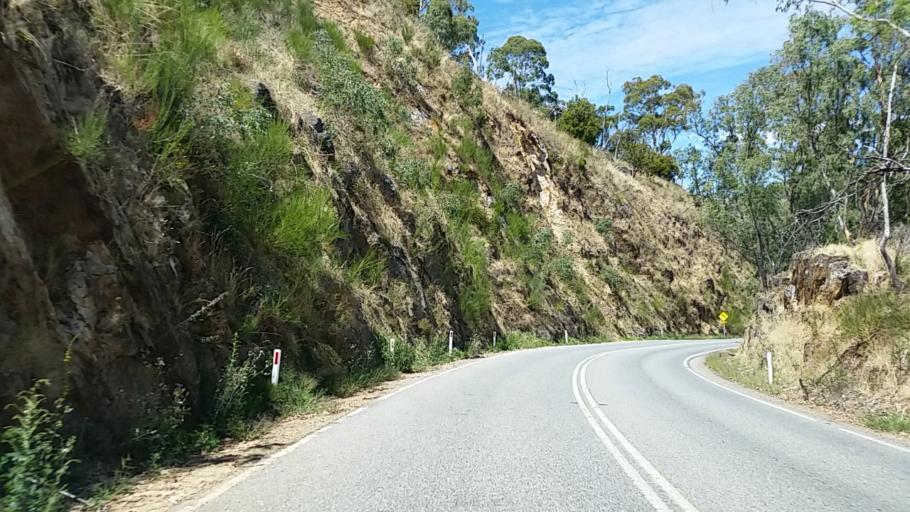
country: AU
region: South Australia
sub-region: Tea Tree Gully
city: Golden Grove
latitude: -34.8488
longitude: 138.7959
